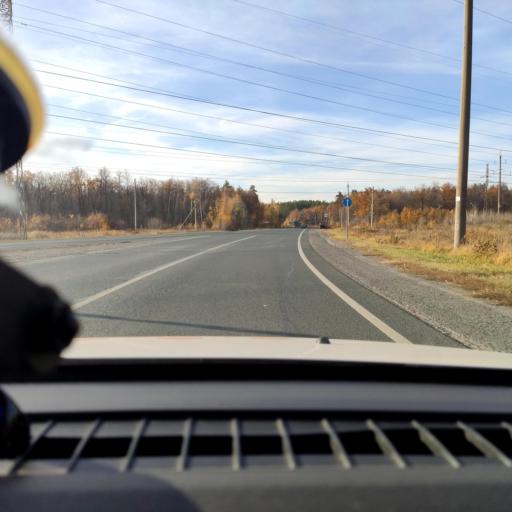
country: RU
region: Samara
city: Volzhskiy
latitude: 53.4511
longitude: 50.1256
